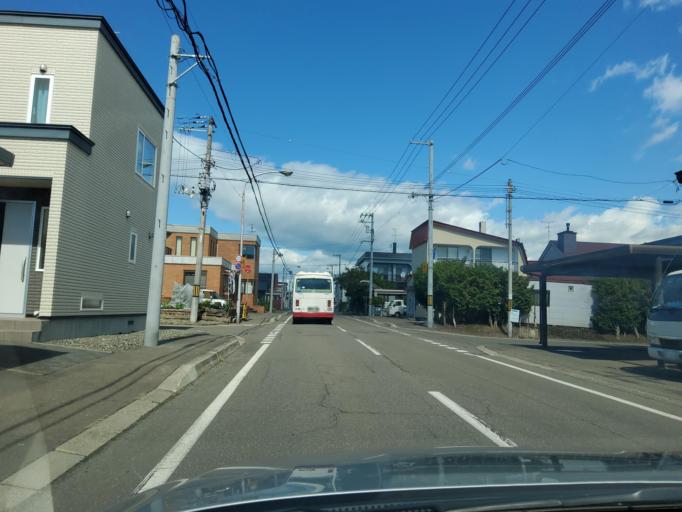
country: JP
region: Hokkaido
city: Obihiro
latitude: 42.9540
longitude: 143.2023
